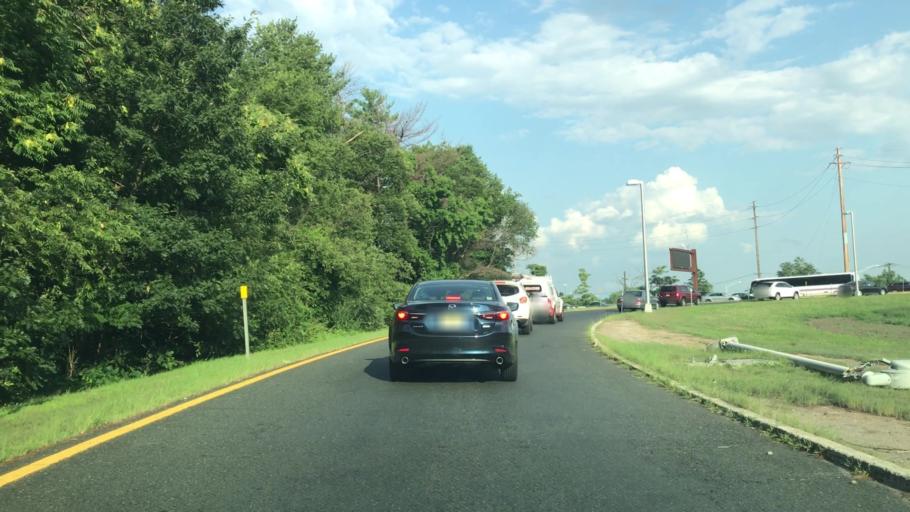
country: US
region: New Jersey
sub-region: Bergen County
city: Rochelle Park
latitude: 40.9240
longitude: -74.0802
